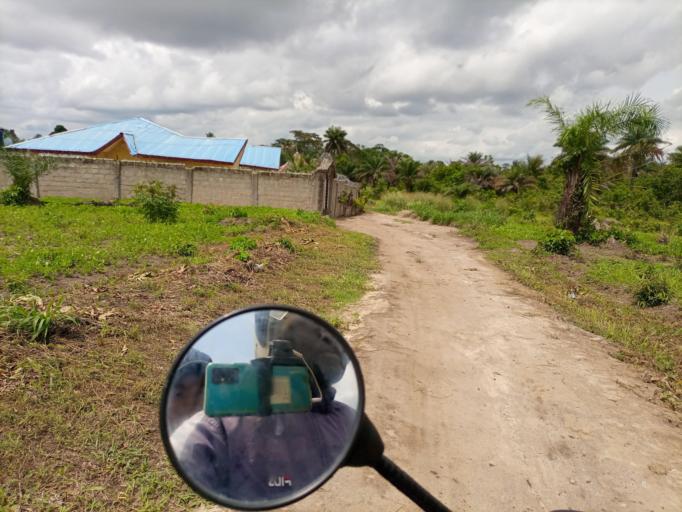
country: SL
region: Southern Province
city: Bo
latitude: 7.9765
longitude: -11.7698
